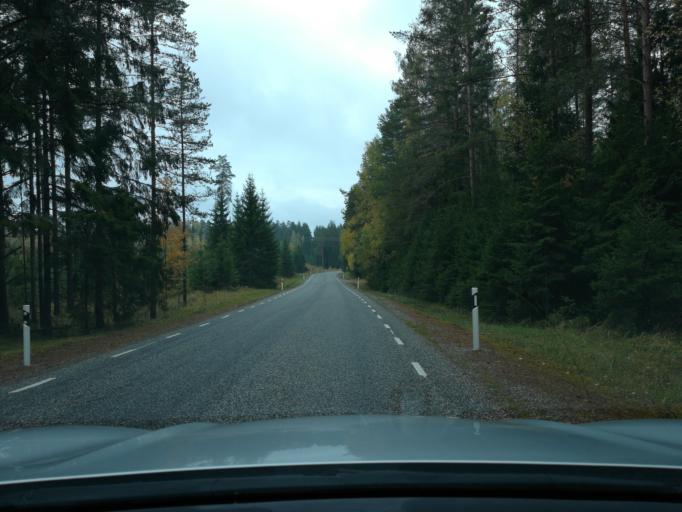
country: EE
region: Ida-Virumaa
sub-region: Johvi vald
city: Johvi
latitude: 59.1792
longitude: 27.4575
